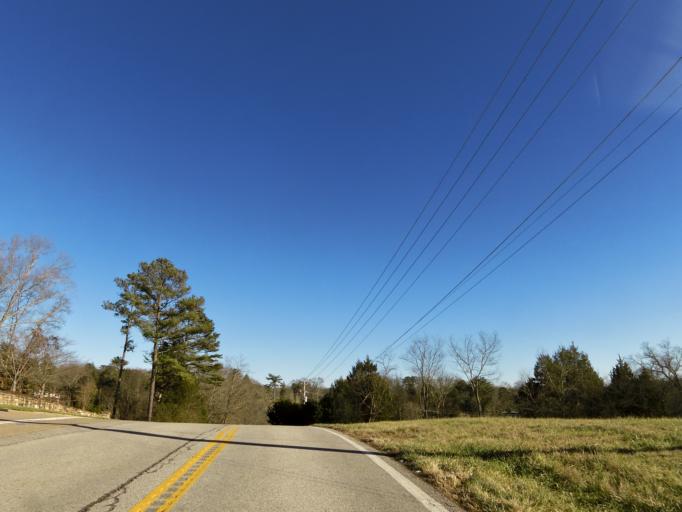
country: US
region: Tennessee
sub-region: Blount County
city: Louisville
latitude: 35.8905
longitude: -83.9906
